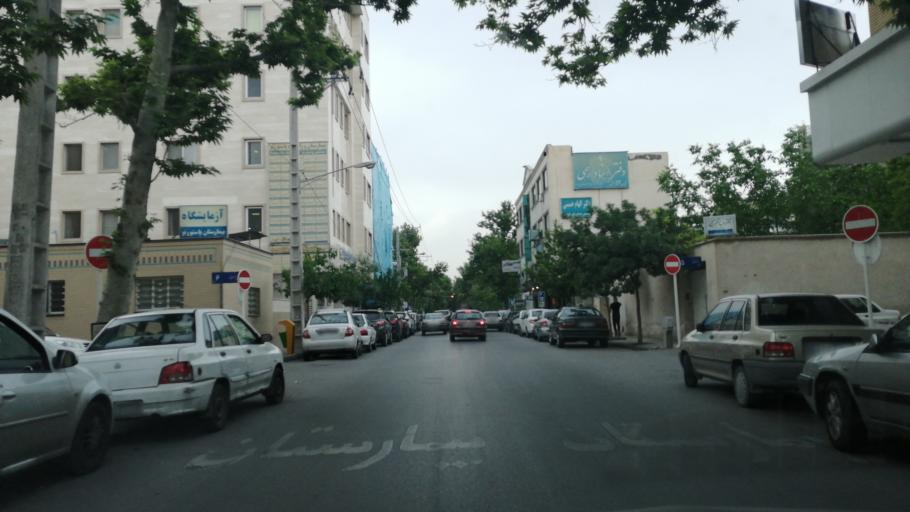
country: IR
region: Razavi Khorasan
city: Mashhad
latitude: 36.2948
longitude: 59.5814
